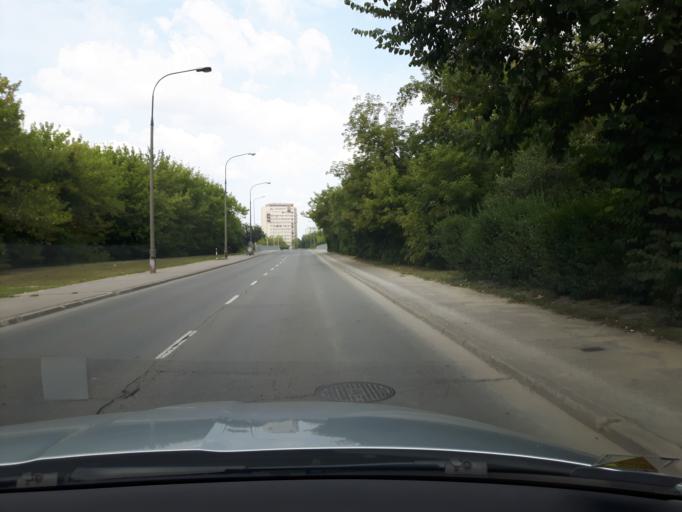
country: PL
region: Masovian Voivodeship
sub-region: Warszawa
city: Wilanow
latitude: 52.1911
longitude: 21.0734
